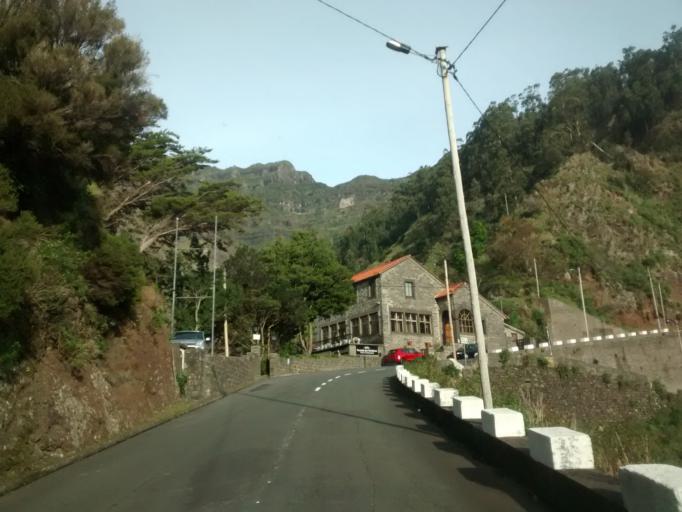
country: PT
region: Madeira
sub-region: Camara de Lobos
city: Curral das Freiras
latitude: 32.7358
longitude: -17.0253
